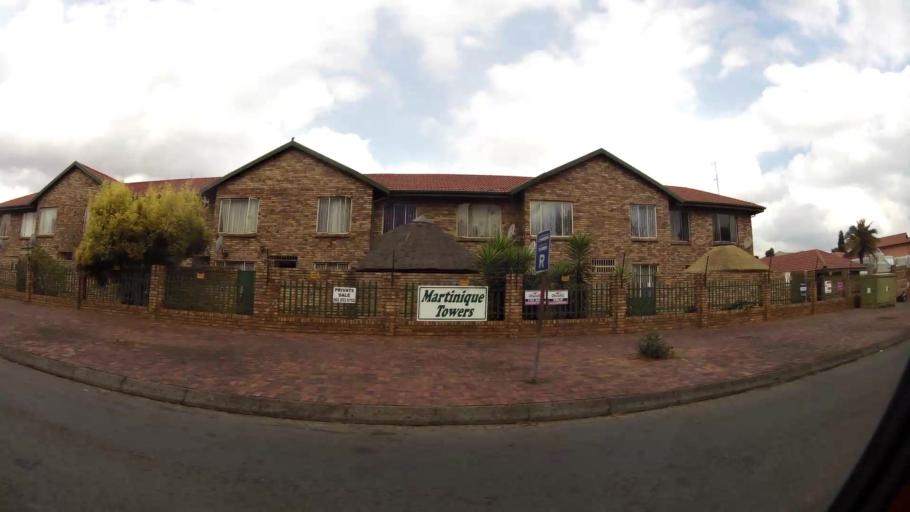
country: ZA
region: Gauteng
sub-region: Sedibeng District Municipality
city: Vanderbijlpark
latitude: -26.7320
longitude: 27.8474
